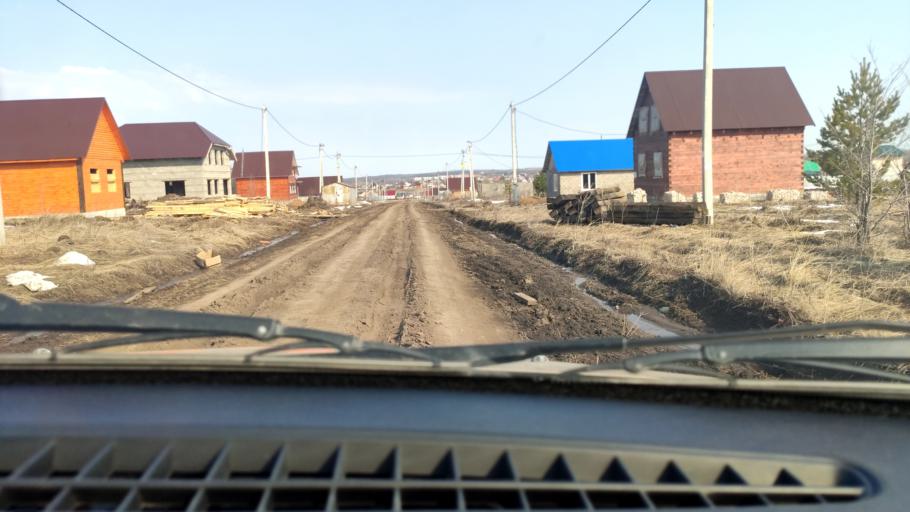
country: RU
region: Bashkortostan
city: Iglino
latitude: 54.7954
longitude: 56.4028
